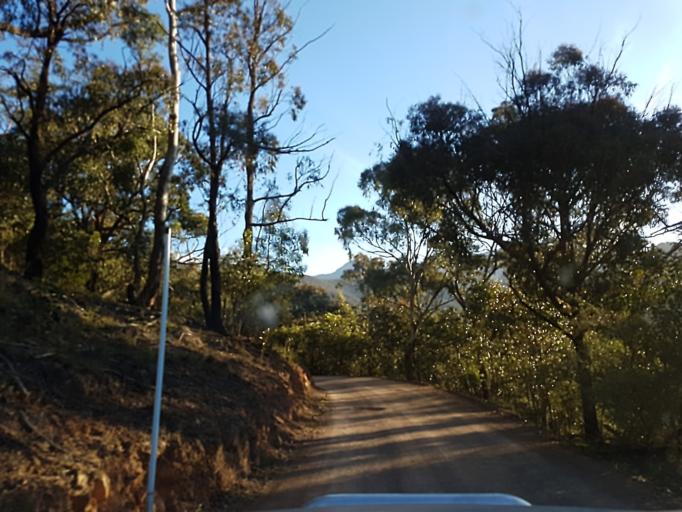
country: AU
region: Victoria
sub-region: Wellington
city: Heyfield
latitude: -37.4029
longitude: 147.0962
